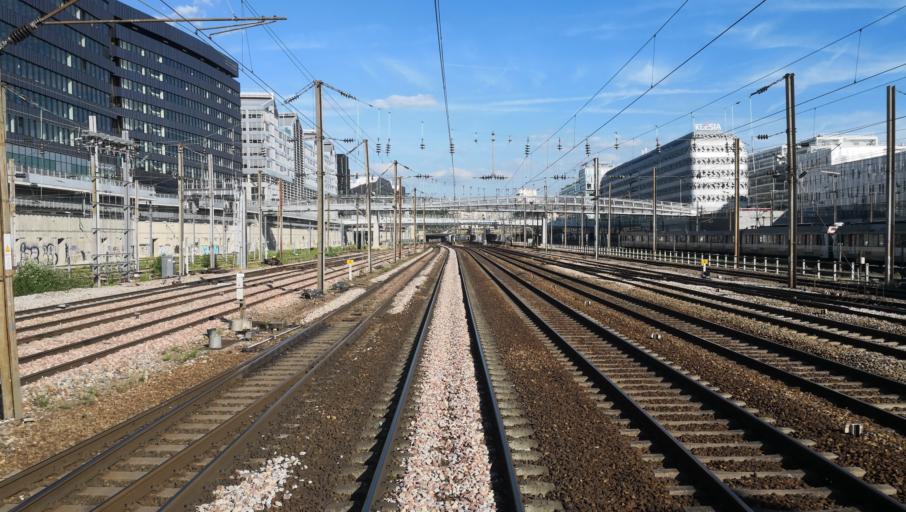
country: FR
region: Ile-de-France
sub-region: Departement des Hauts-de-Seine
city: Clichy
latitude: 48.8889
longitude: 2.3151
